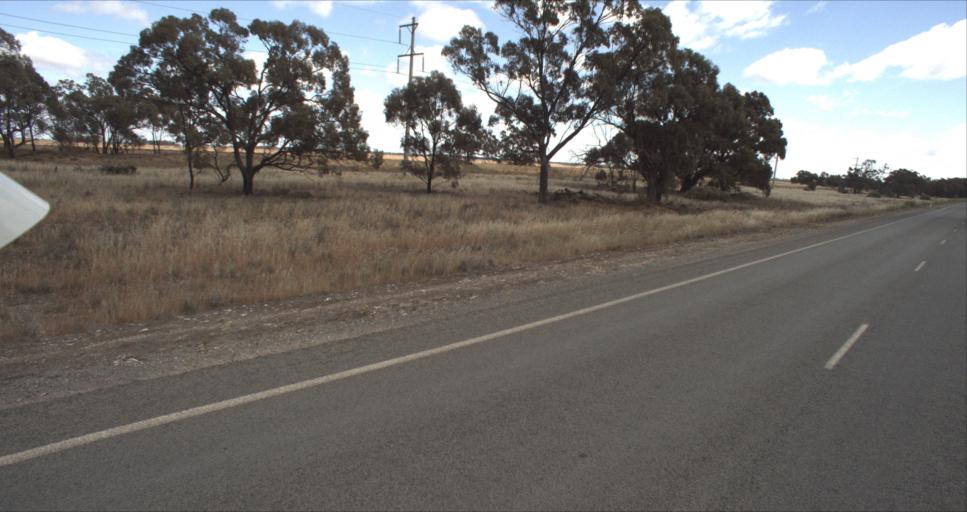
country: AU
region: New South Wales
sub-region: Murrumbidgee Shire
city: Darlington Point
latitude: -34.5716
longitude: 146.1671
